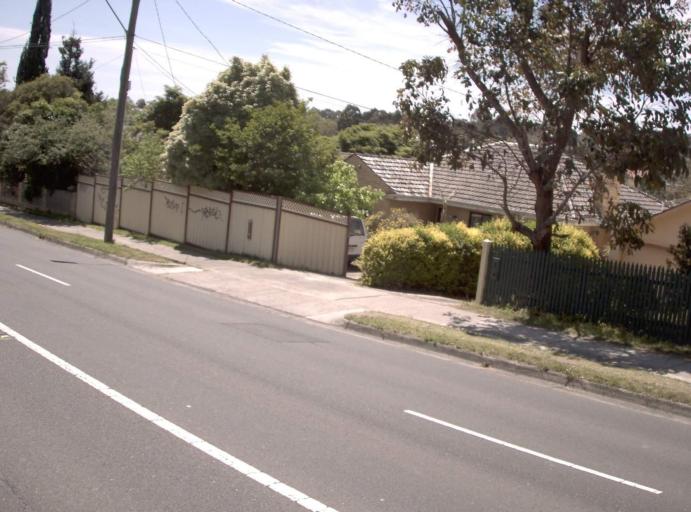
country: AU
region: Victoria
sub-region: Monash
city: Notting Hill
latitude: -37.8792
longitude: 145.1470
